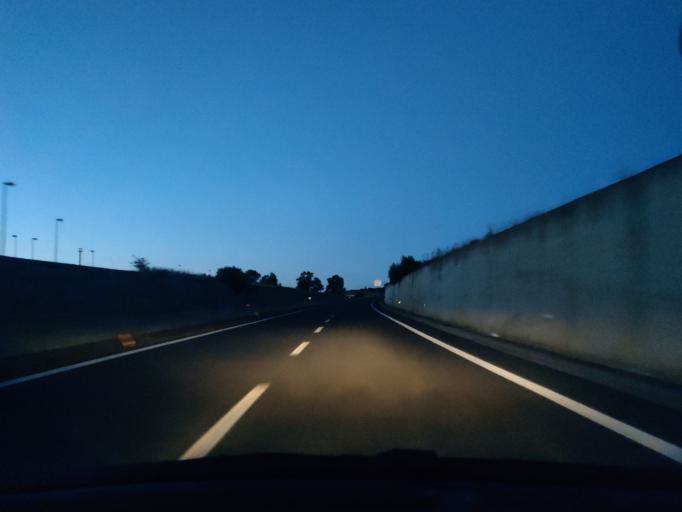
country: IT
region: Latium
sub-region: Citta metropolitana di Roma Capitale
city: Aurelia
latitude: 42.1236
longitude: 11.7911
